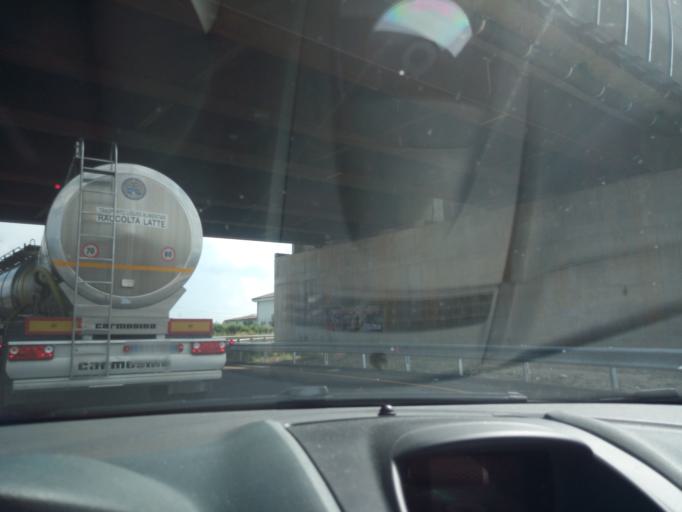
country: IT
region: Calabria
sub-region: Provincia di Cosenza
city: San Lorenzo del Vallo
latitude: 39.7220
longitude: 16.2434
